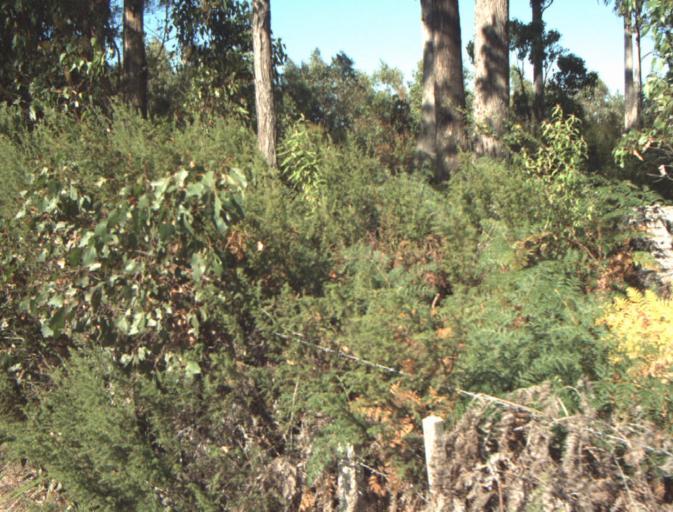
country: AU
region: Tasmania
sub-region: Dorset
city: Scottsdale
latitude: -41.2978
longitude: 147.3547
